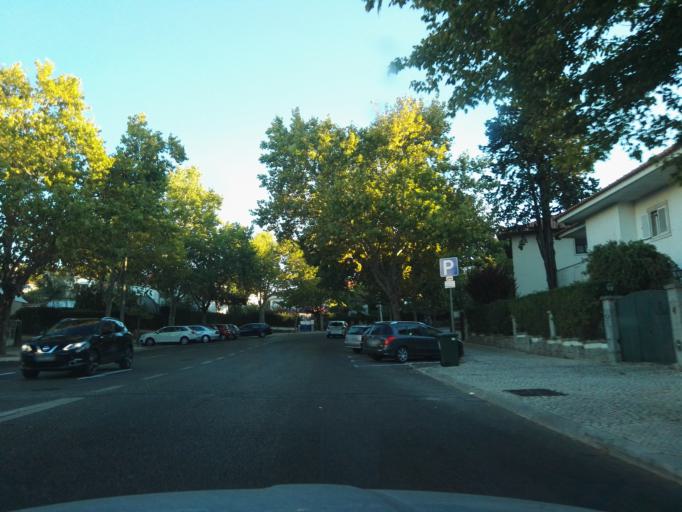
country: PT
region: Lisbon
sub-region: Lisbon
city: Lisbon
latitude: 38.7547
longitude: -9.1365
